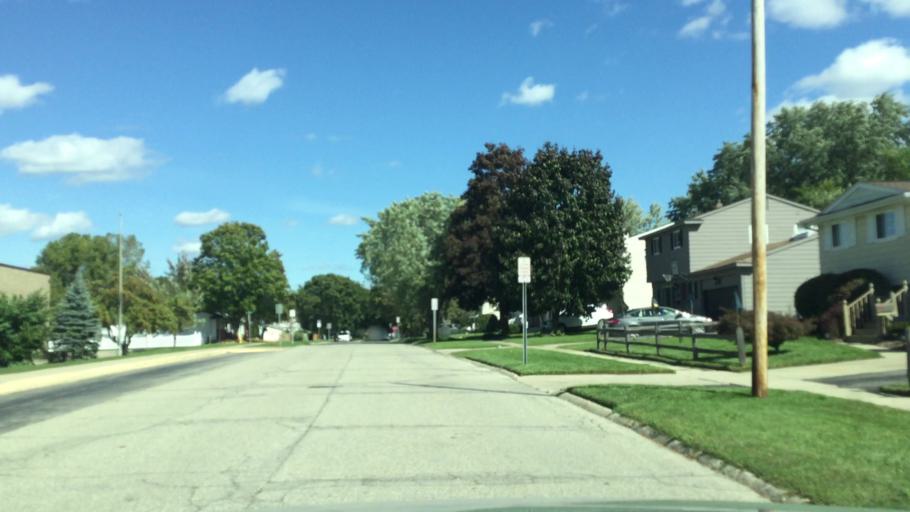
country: US
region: Michigan
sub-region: Genesee County
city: Swartz Creek
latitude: 42.9501
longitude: -83.8519
